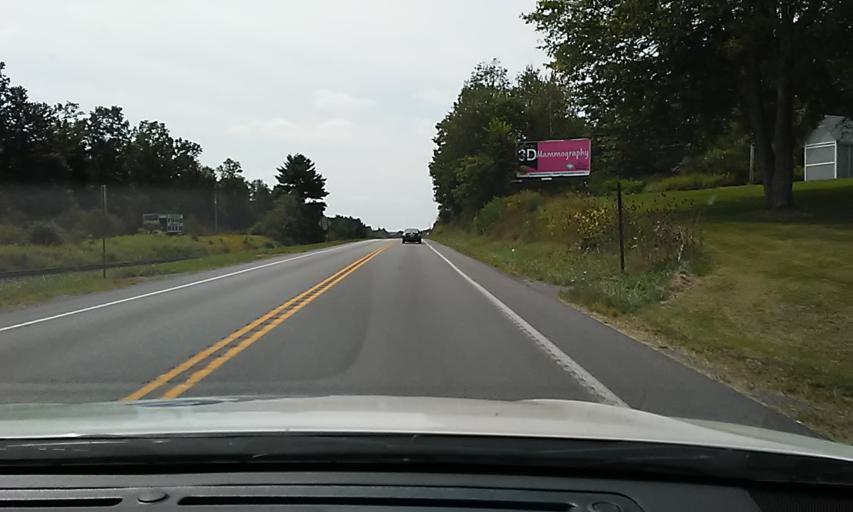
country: US
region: Pennsylvania
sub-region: Clearfield County
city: Treasure Lake
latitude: 41.1352
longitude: -78.6991
